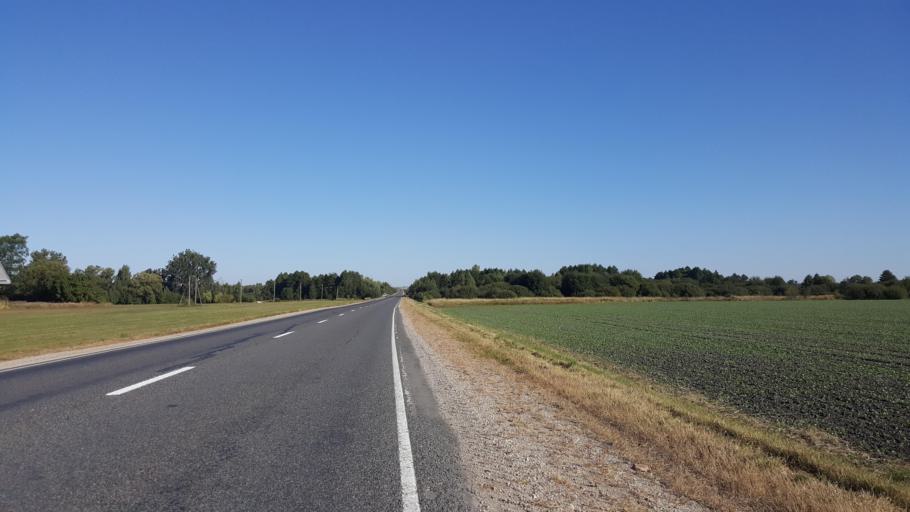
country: BY
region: Brest
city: Kamyanyets
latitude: 52.3831
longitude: 23.7882
